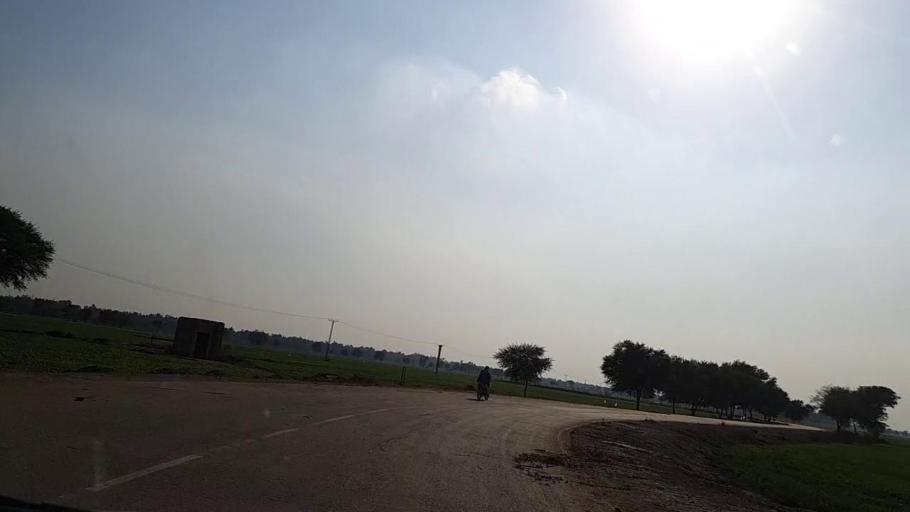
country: PK
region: Sindh
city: Sakrand
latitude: 26.1178
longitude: 68.2497
